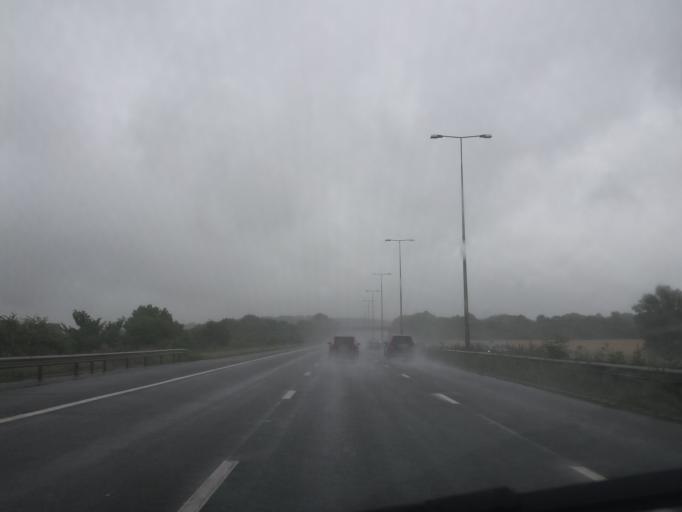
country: GB
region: England
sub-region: Leicestershire
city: Shepshed
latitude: 52.7794
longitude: -1.2805
